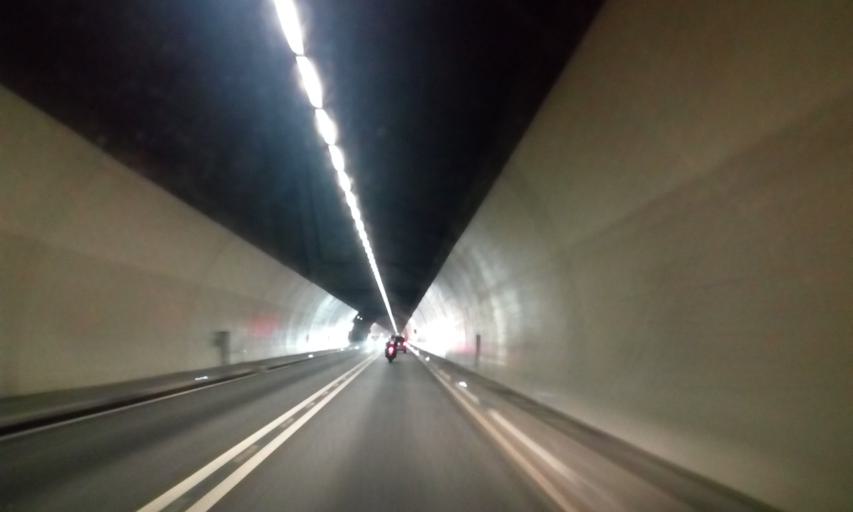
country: CH
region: Grisons
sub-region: Imboden District
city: Bonaduz
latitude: 46.8299
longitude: 9.3572
